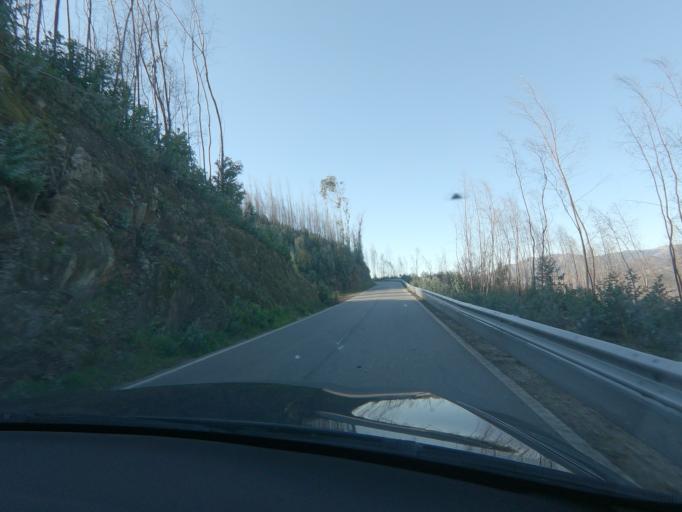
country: PT
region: Viseu
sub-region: Vouzela
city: Vouzela
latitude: 40.7290
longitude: -8.1367
